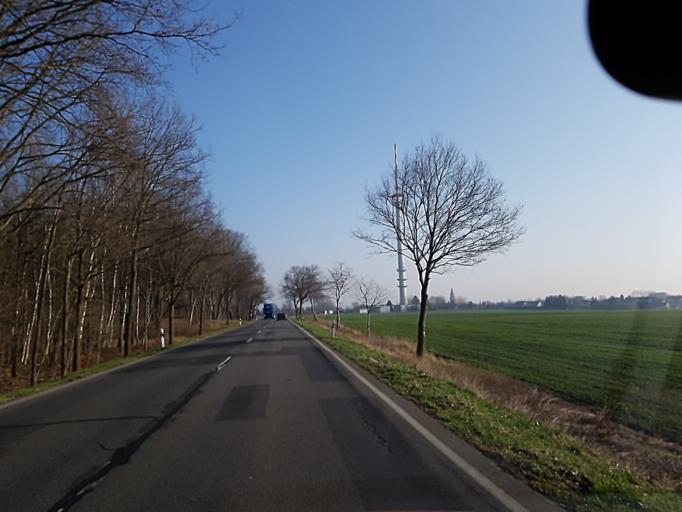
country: DE
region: Brandenburg
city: Calau
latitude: 51.7373
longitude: 13.9377
